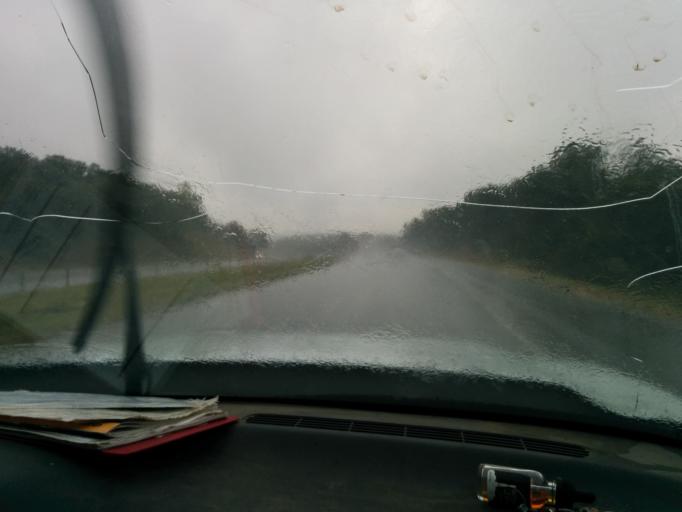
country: US
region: Oklahoma
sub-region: Okmulgee County
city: Beggs
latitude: 35.7316
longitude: -96.0045
